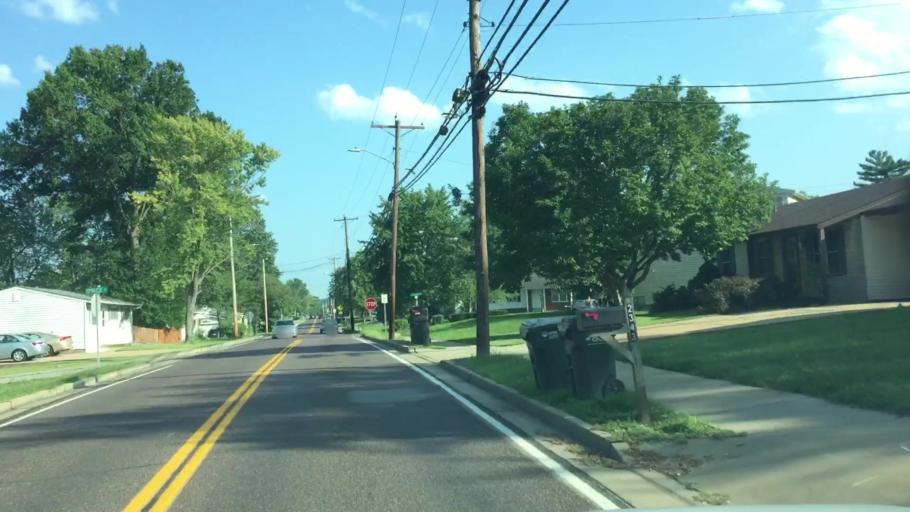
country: US
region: Missouri
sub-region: Jefferson County
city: Arnold
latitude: 38.4473
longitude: -90.3562
